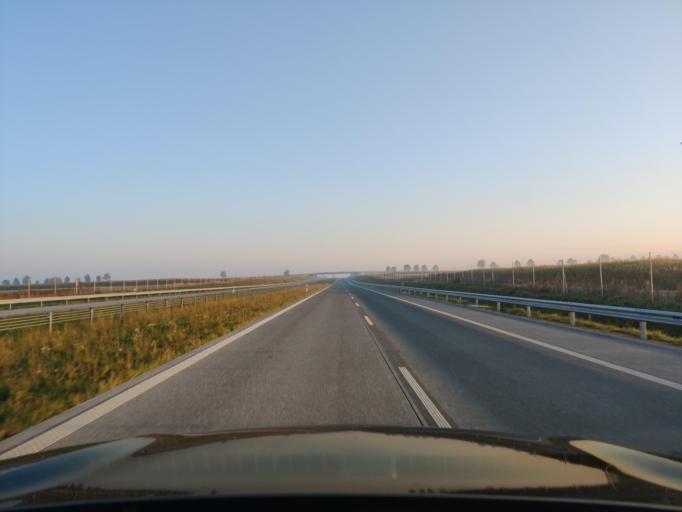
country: PL
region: Masovian Voivodeship
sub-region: Powiat mlawski
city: Wisniewo
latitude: 53.0548
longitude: 20.3633
